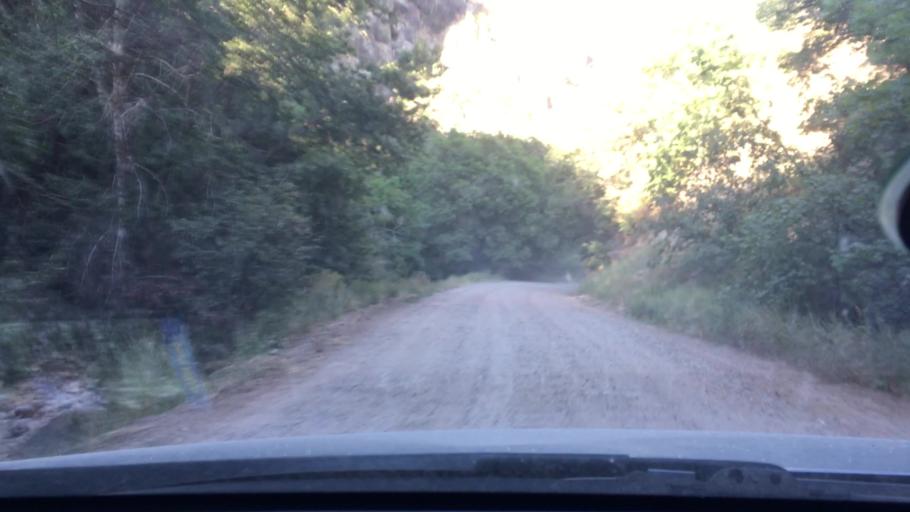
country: US
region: Utah
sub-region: Sanpete County
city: Fountain Green
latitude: 39.5552
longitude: -111.6685
